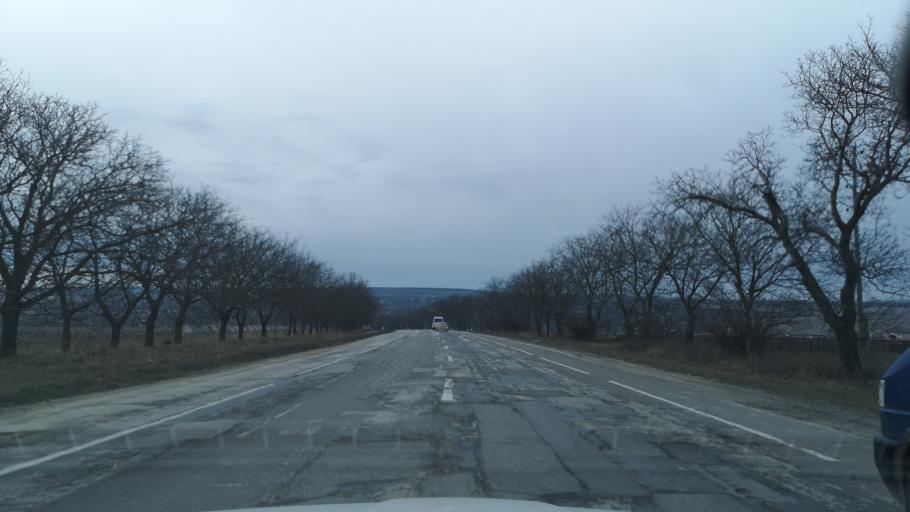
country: RO
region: Botosani
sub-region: Comuna Radauti-Prut
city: Miorcani
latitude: 48.3063
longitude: 26.9478
